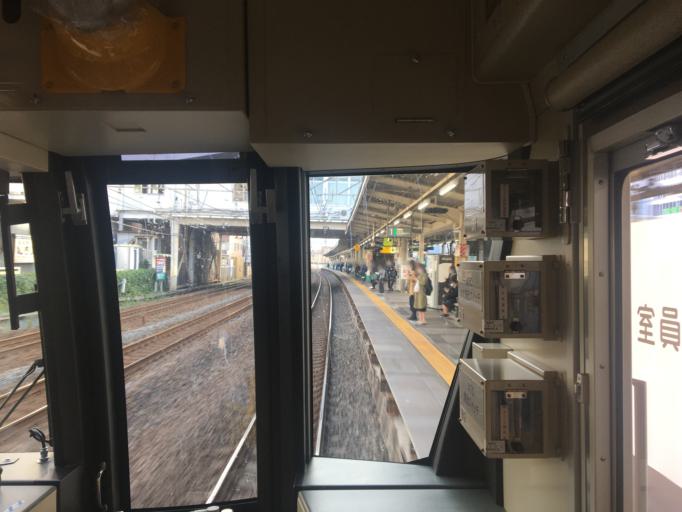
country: JP
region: Chiba
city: Kashiwa
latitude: 35.8443
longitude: 139.9536
